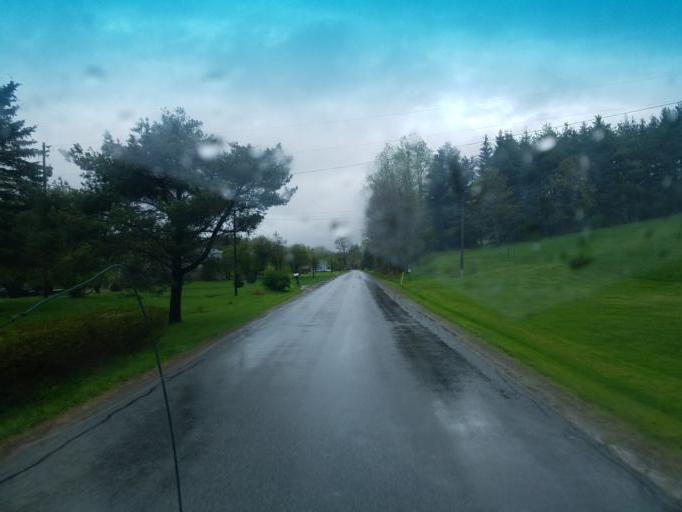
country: US
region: Pennsylvania
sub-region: Tioga County
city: Westfield
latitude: 41.9494
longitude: -77.6474
